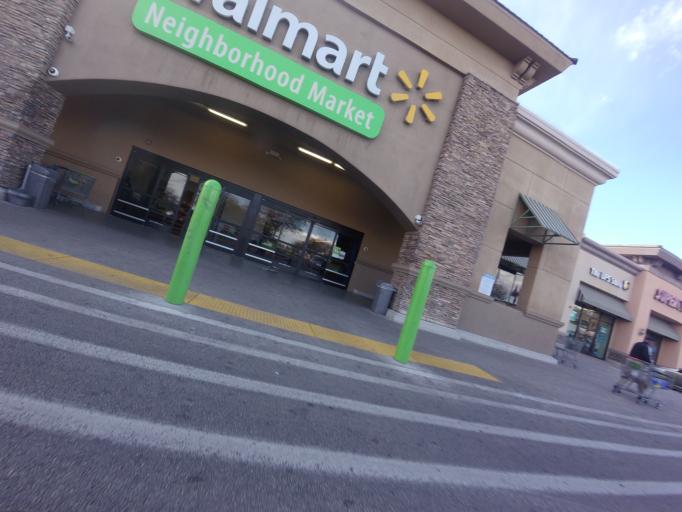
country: US
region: Nevada
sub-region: Clark County
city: North Las Vegas
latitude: 36.2605
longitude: -115.1813
